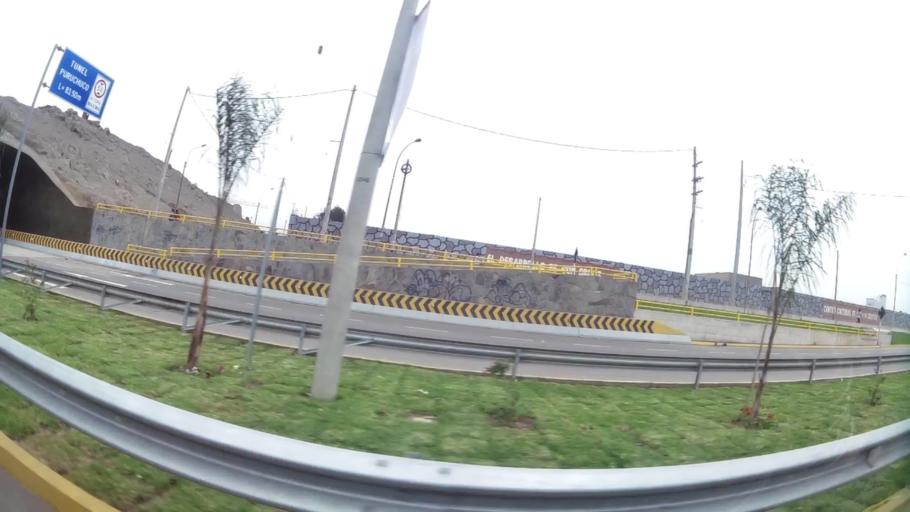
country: PE
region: Lima
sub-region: Lima
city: Vitarte
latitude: -12.0438
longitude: -76.9325
